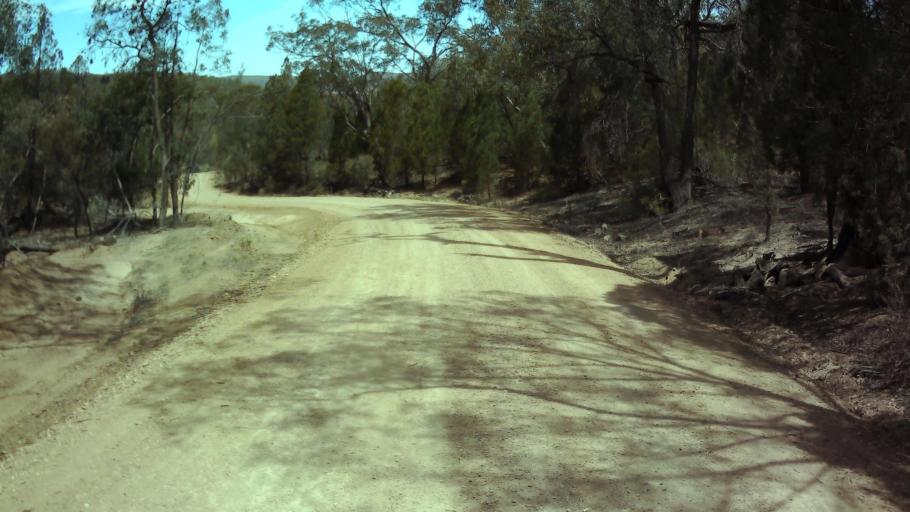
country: AU
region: New South Wales
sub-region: Weddin
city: Grenfell
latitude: -33.8134
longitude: 148.1624
